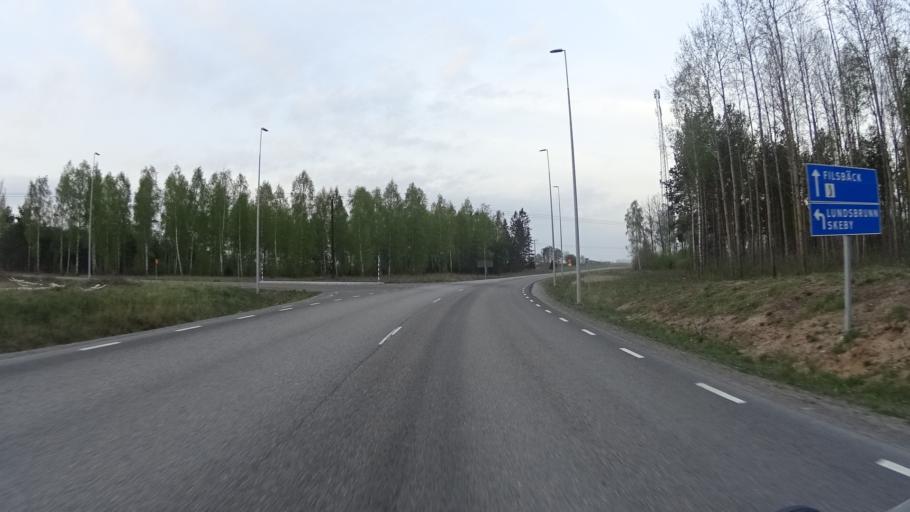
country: SE
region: Vaestra Goetaland
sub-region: Gotene Kommun
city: Kallby
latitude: 58.4984
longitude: 13.3050
